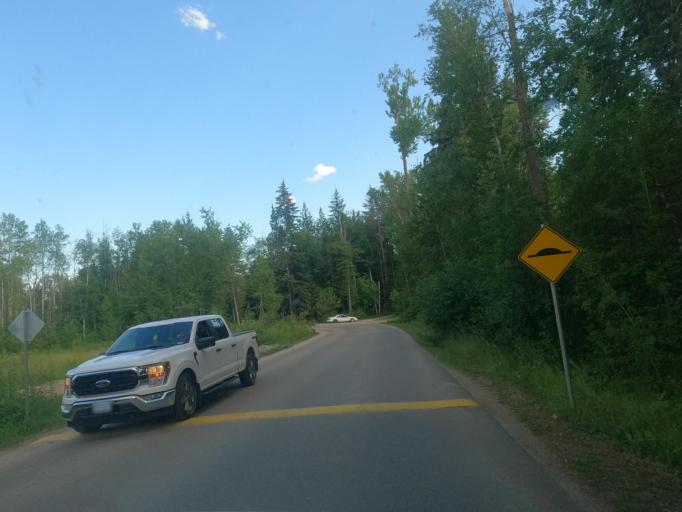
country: CA
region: British Columbia
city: Salmon Arm
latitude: 50.7307
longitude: -119.3132
